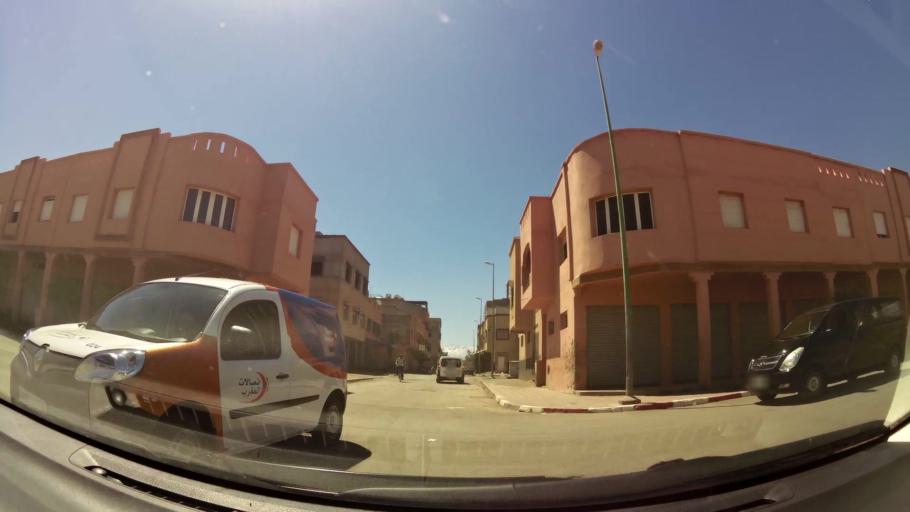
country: MA
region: Marrakech-Tensift-Al Haouz
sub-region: Marrakech
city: Marrakesh
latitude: 31.5716
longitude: -7.9828
